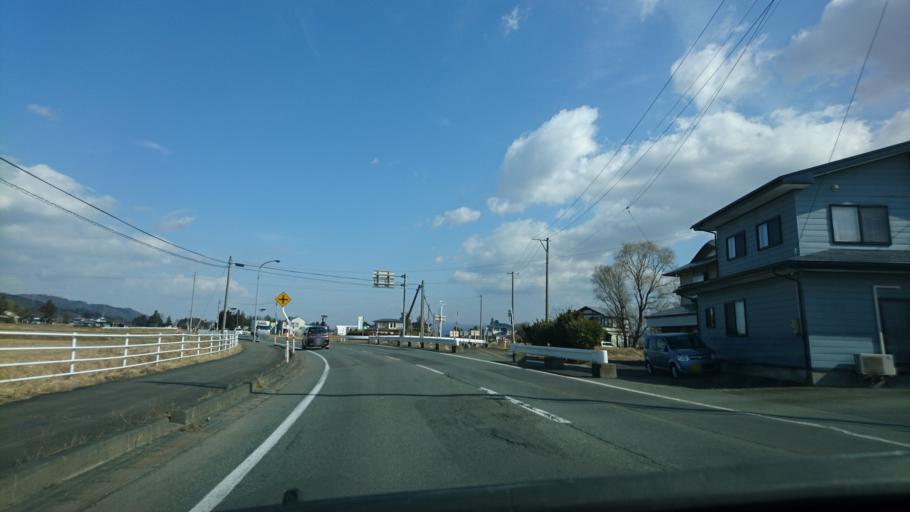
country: JP
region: Iwate
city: Morioka-shi
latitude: 39.5693
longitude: 141.1093
